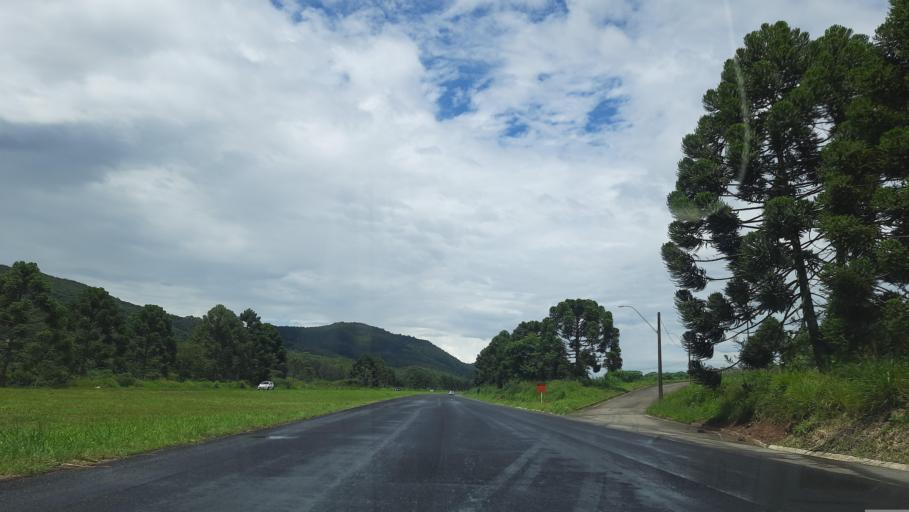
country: BR
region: Minas Gerais
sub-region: Pocos De Caldas
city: Pocos de Caldas
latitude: -21.8192
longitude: -46.6634
